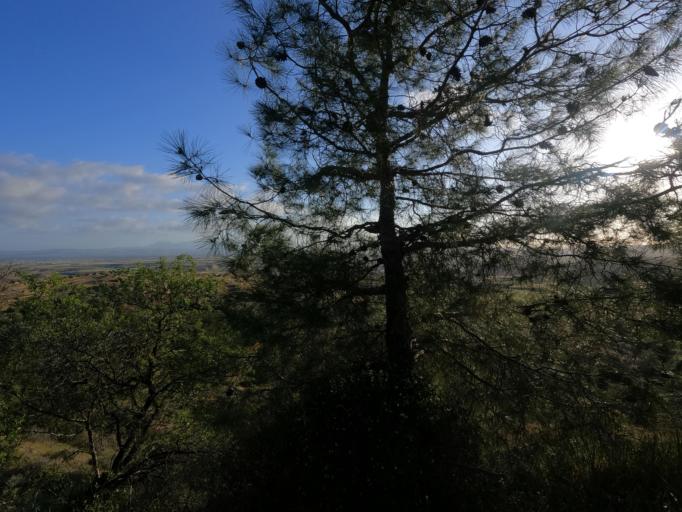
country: CY
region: Lefkosia
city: Astromeritis
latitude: 35.0680
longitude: 33.0377
